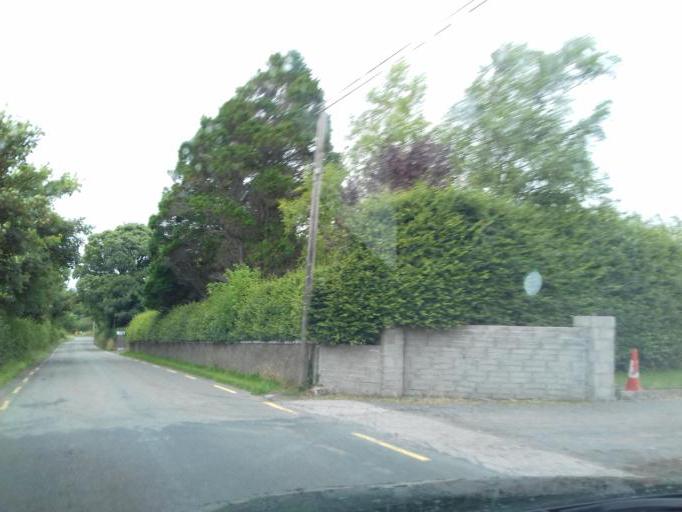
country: IE
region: Leinster
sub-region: County Carlow
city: Bagenalstown
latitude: 52.6238
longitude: -7.0408
